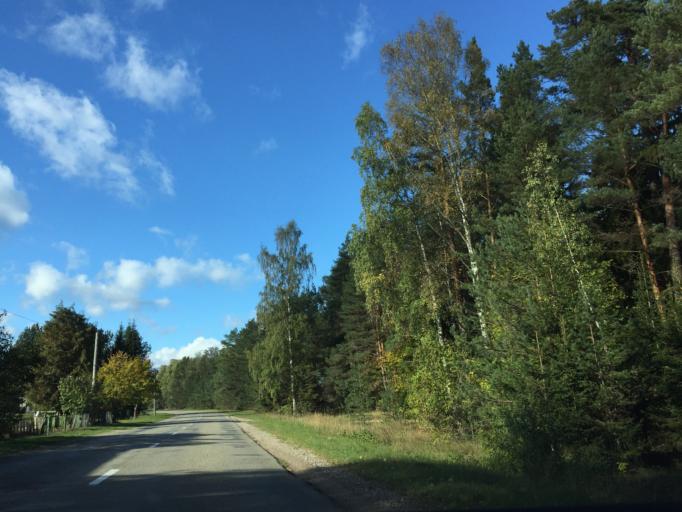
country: LV
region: Rojas
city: Roja
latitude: 57.4065
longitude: 22.9553
